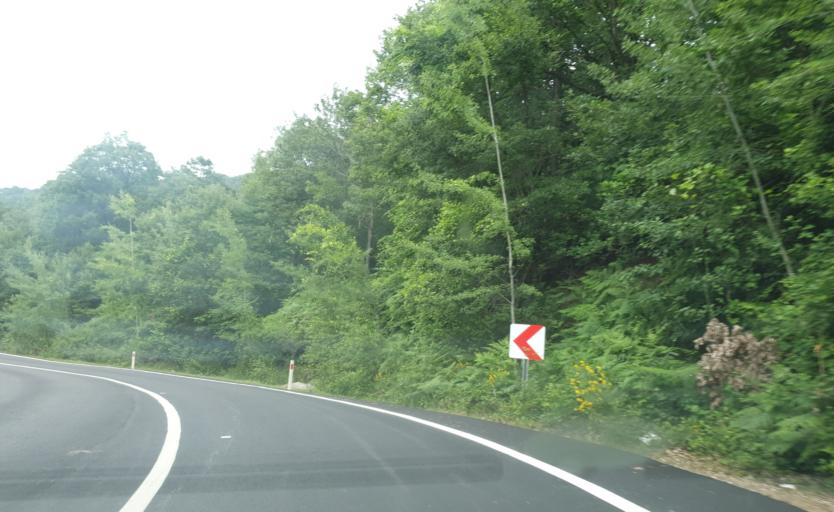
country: TR
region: Kirklareli
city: Salmydessus
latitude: 41.5987
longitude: 28.0876
